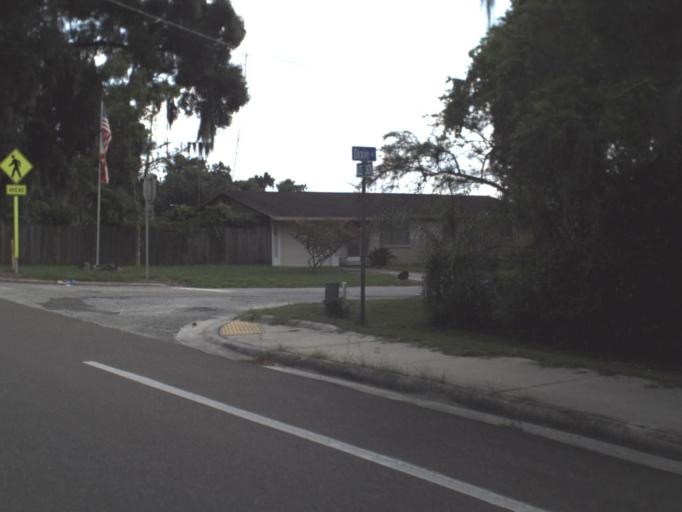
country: US
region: Florida
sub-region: Pasco County
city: Dade City
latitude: 28.3542
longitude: -82.1875
